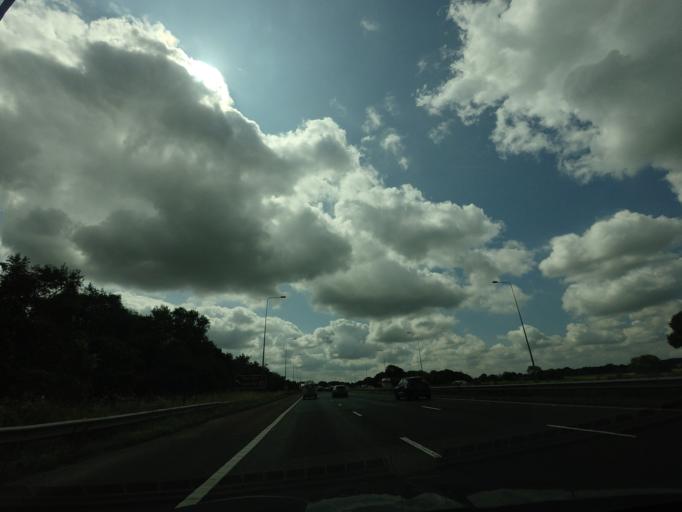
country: GB
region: England
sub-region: Borough of Wigan
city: Shevington
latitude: 53.6057
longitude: -2.6894
